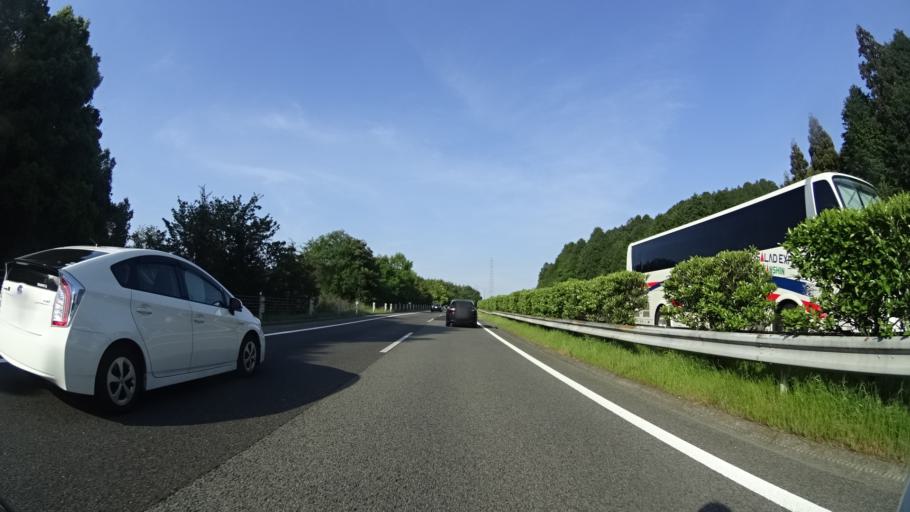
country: JP
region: Ehime
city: Niihama
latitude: 33.9120
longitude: 133.2690
